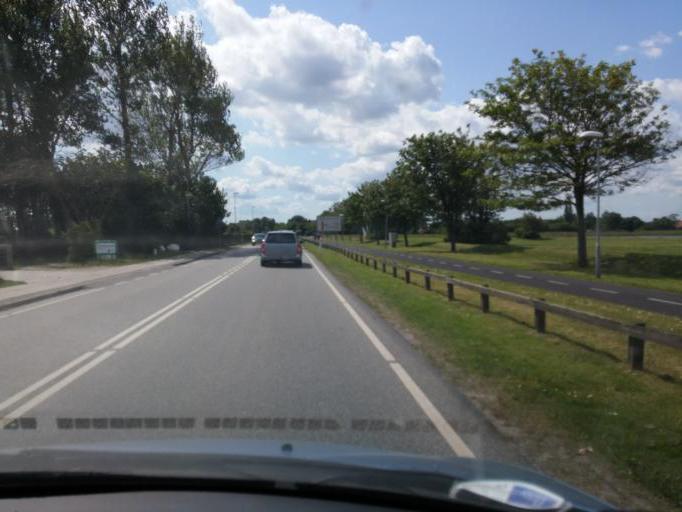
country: DK
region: South Denmark
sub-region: Kerteminde Kommune
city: Kerteminde
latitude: 55.4446
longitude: 10.6578
